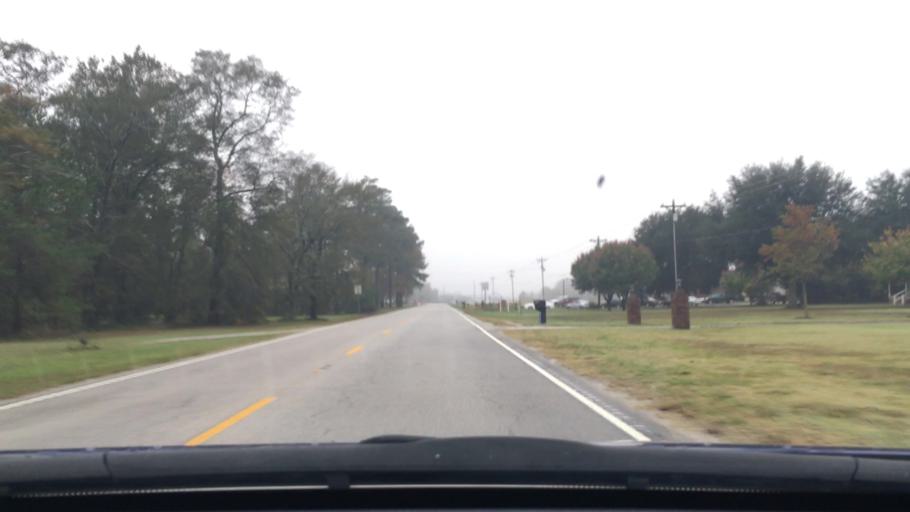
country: US
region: South Carolina
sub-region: Florence County
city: Timmonsville
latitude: 34.2126
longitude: -80.0183
